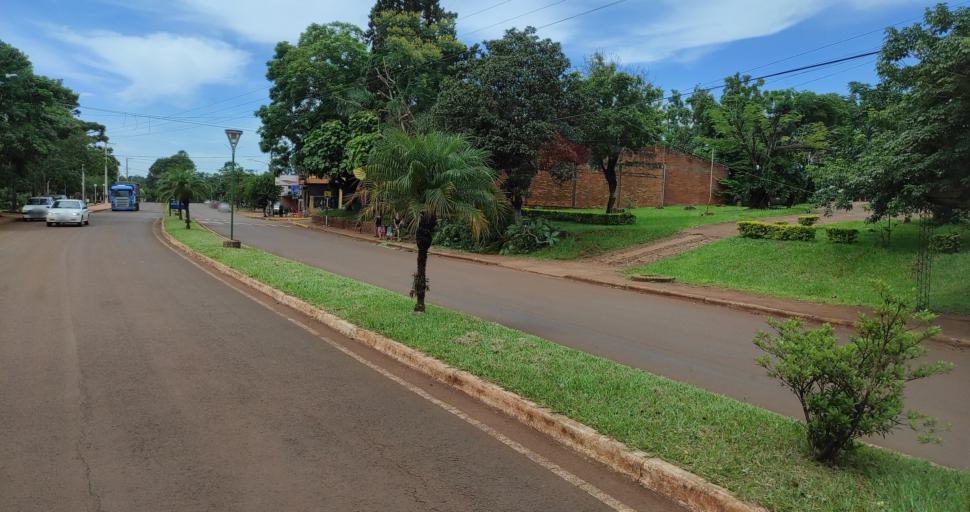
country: AR
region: Misiones
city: El Alcazar
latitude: -26.7151
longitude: -54.8142
